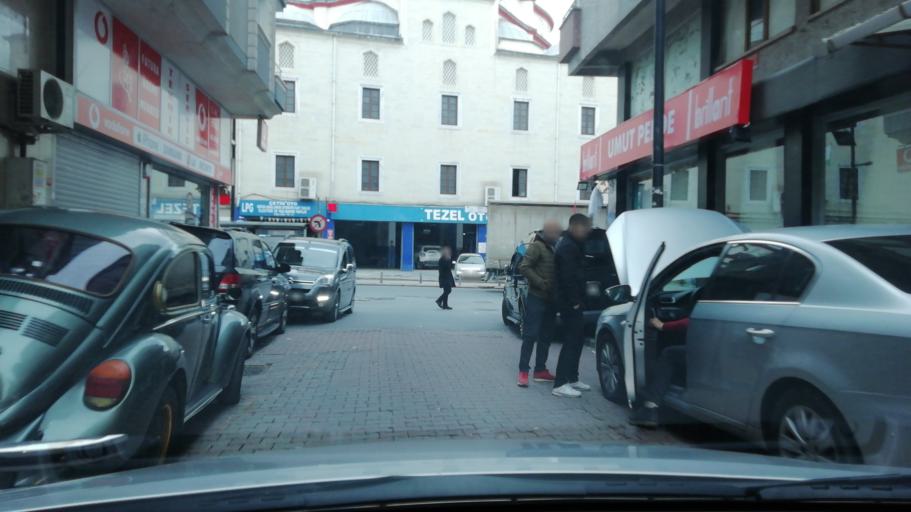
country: TR
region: Istanbul
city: Bahcelievler
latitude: 41.0092
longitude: 28.8385
